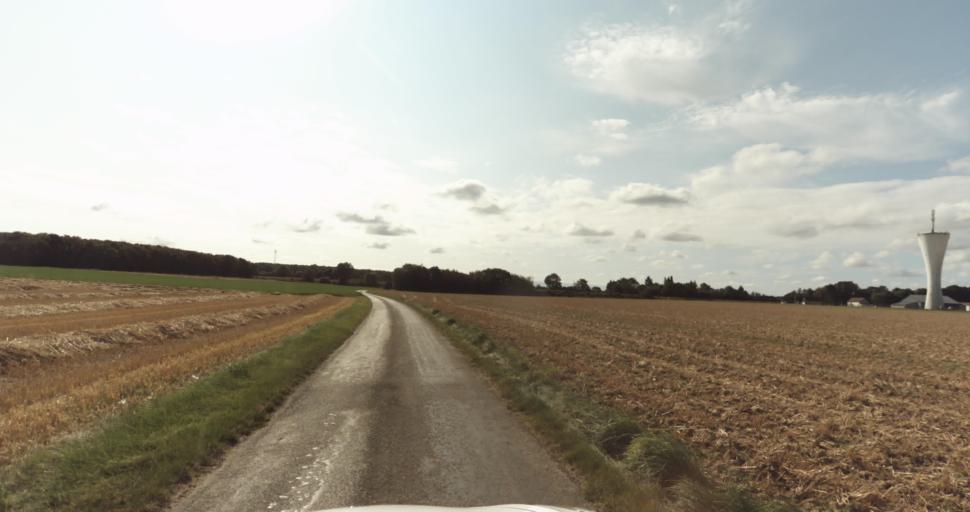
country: FR
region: Haute-Normandie
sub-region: Departement de l'Eure
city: Tillieres-sur-Avre
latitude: 48.7782
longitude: 1.0787
